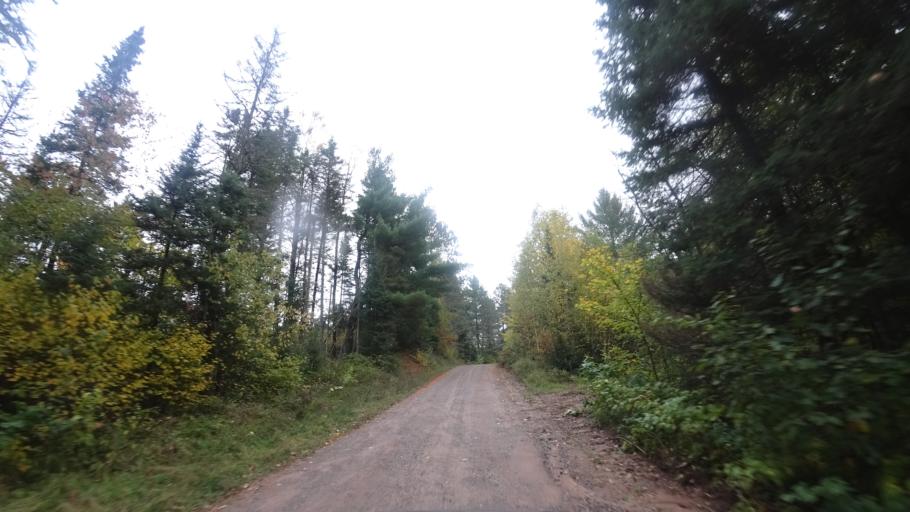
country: US
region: Wisconsin
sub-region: Sawyer County
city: Little Round Lake
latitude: 46.0851
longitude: -90.9873
